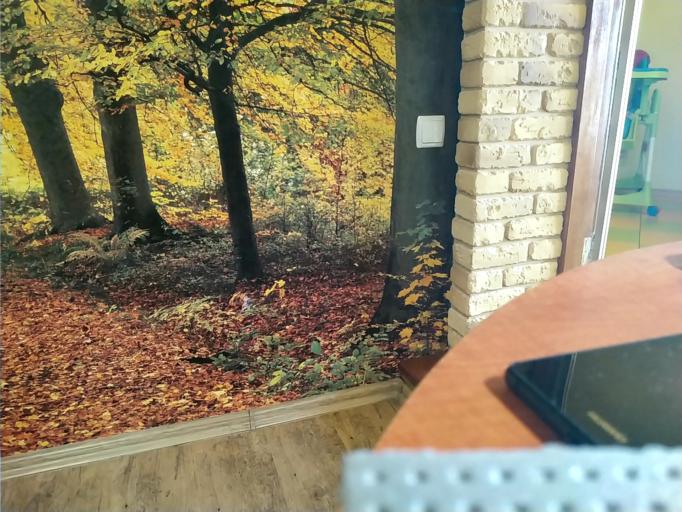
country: RU
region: Kaluga
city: Kondrovo
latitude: 54.7979
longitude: 35.9188
